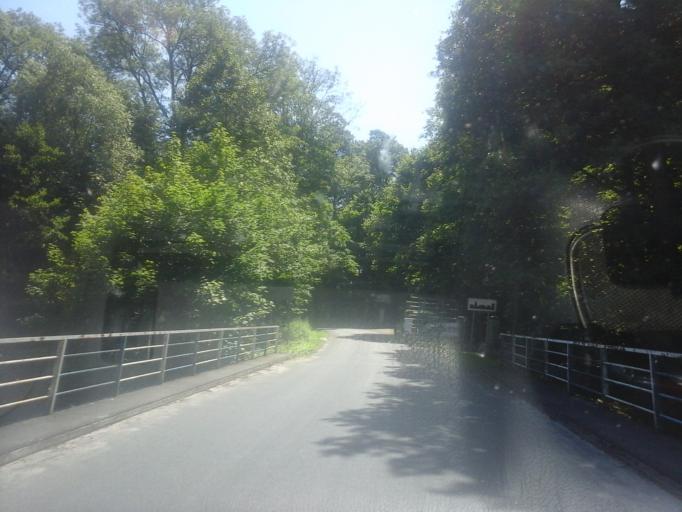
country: PL
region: West Pomeranian Voivodeship
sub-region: Powiat bialogardzki
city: Bialogard
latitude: 54.1059
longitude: 16.0022
